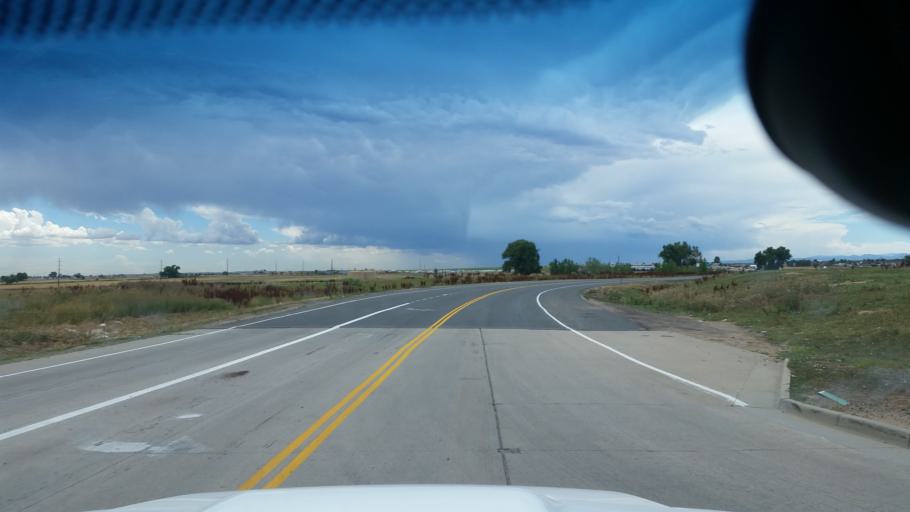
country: US
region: Colorado
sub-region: Weld County
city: Dacono
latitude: 40.0438
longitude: -104.9765
